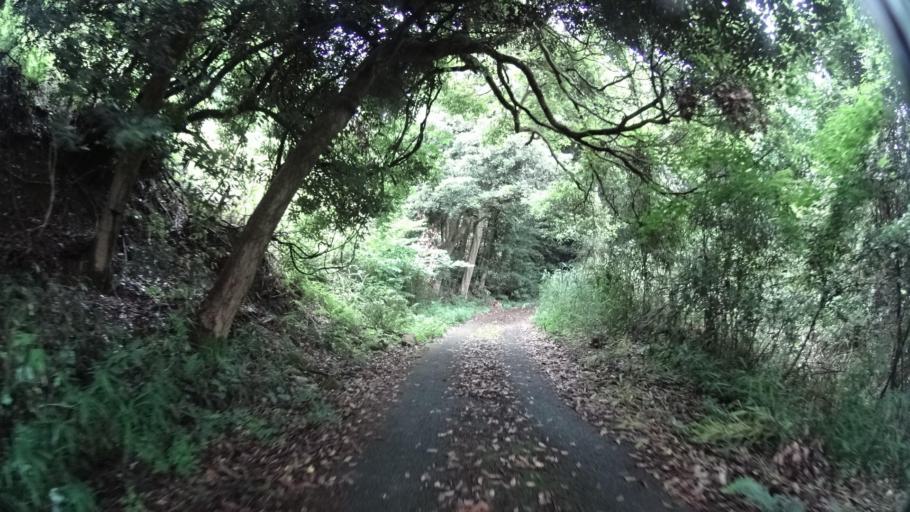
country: JP
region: Kyoto
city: Maizuru
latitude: 35.5337
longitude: 135.3426
